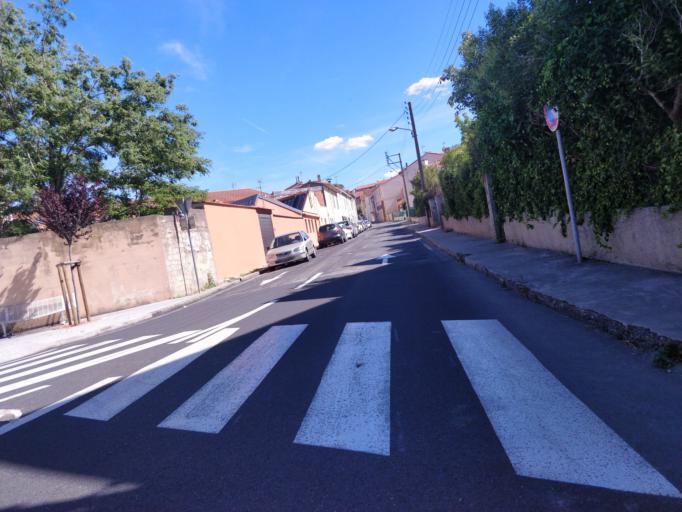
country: FR
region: Languedoc-Roussillon
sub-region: Departement des Pyrenees-Orientales
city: Elne
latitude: 42.6023
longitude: 2.9688
